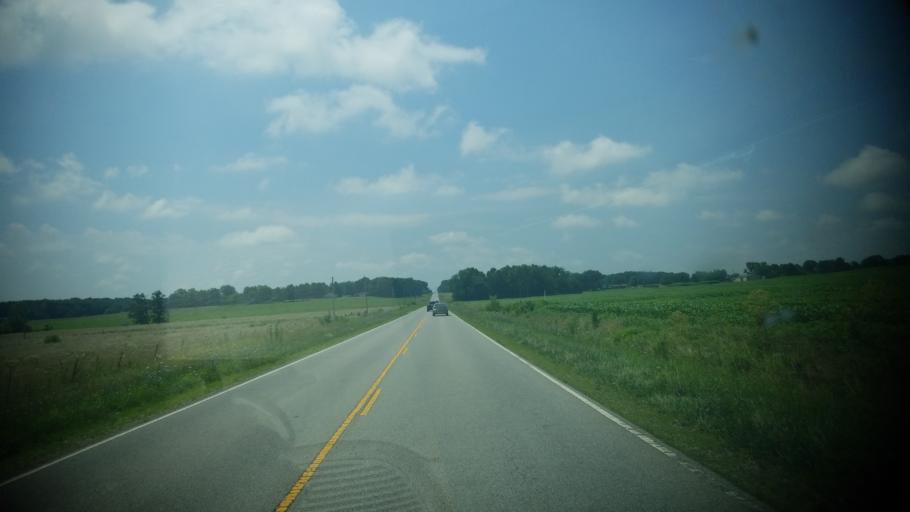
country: US
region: Illinois
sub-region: Wayne County
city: Fairfield
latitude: 38.4222
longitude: -88.3498
